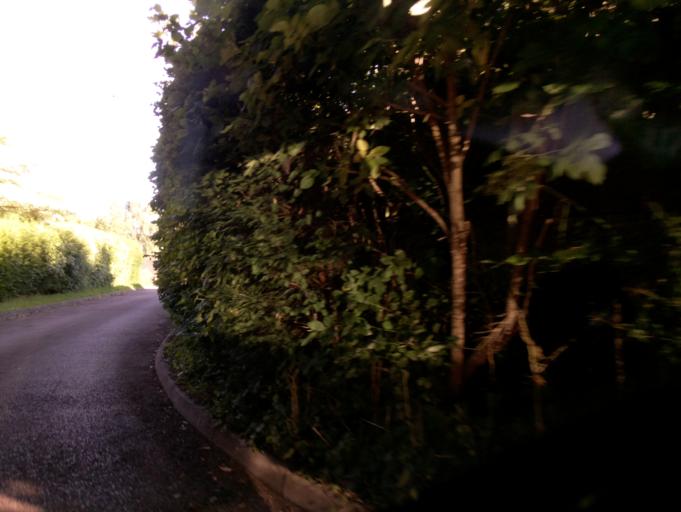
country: GB
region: Wales
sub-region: Monmouthshire
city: Chepstow
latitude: 51.6277
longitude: -2.6968
